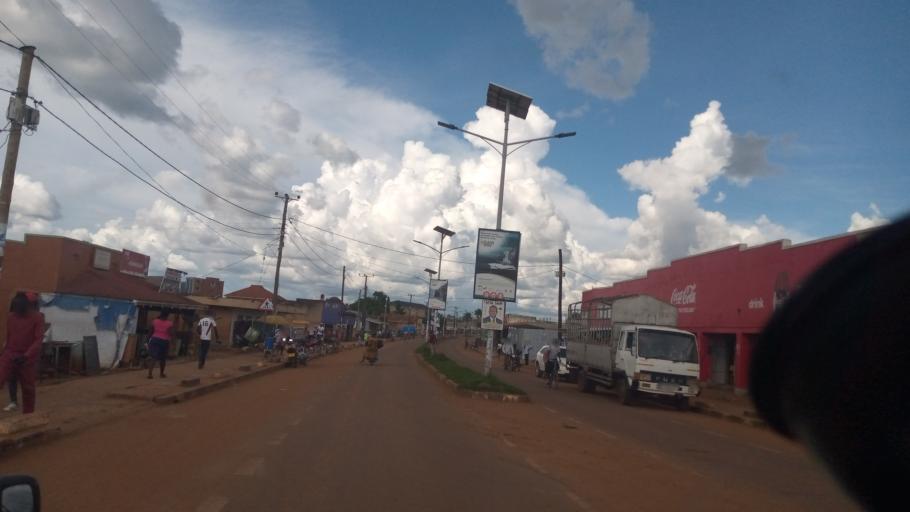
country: UG
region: Northern Region
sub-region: Lira District
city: Lira
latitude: 2.2417
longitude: 32.8901
